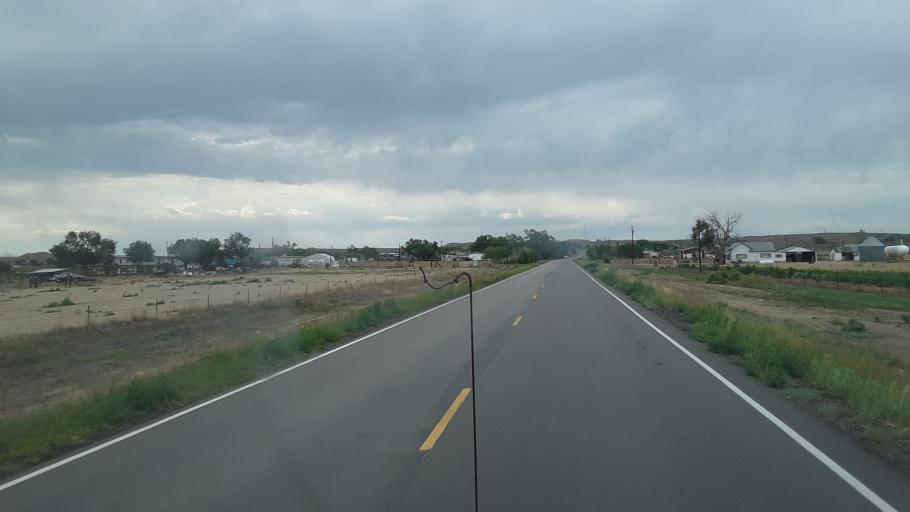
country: US
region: Colorado
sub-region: Otero County
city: Fowler
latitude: 38.1453
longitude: -104.0229
